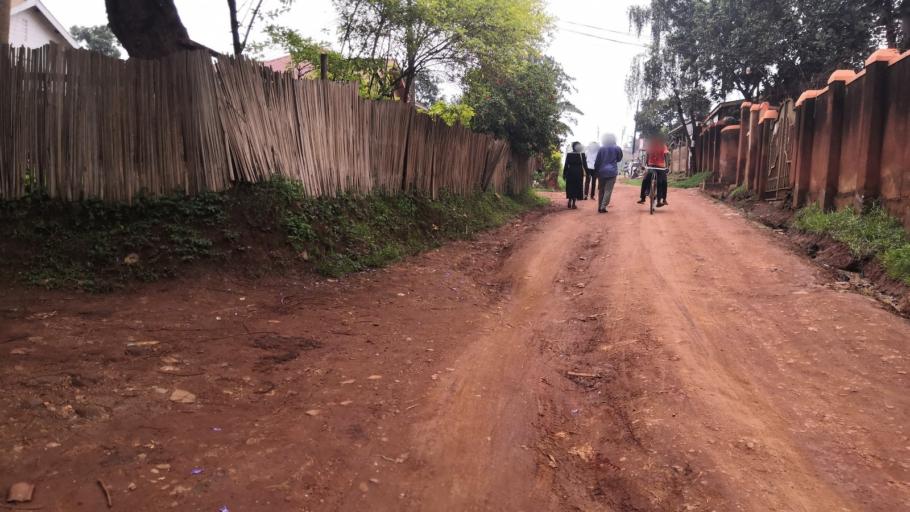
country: UG
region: Central Region
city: Kampala Central Division
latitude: 0.3430
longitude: 32.5621
